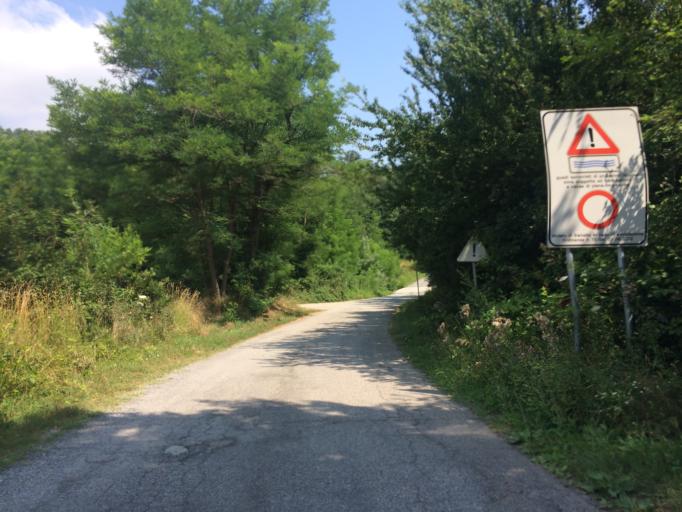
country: IT
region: Piedmont
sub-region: Provincia di Alessandria
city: Pareto
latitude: 44.4895
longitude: 8.3504
